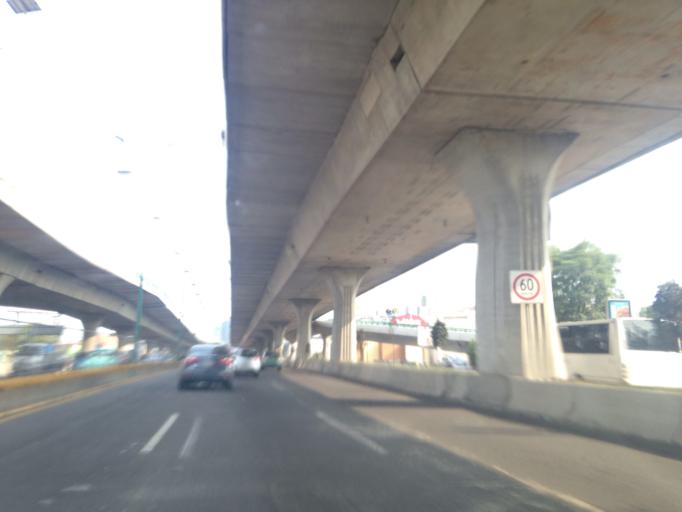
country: MX
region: Mexico
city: Naucalpan de Juarez
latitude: 19.4797
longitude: -99.2320
